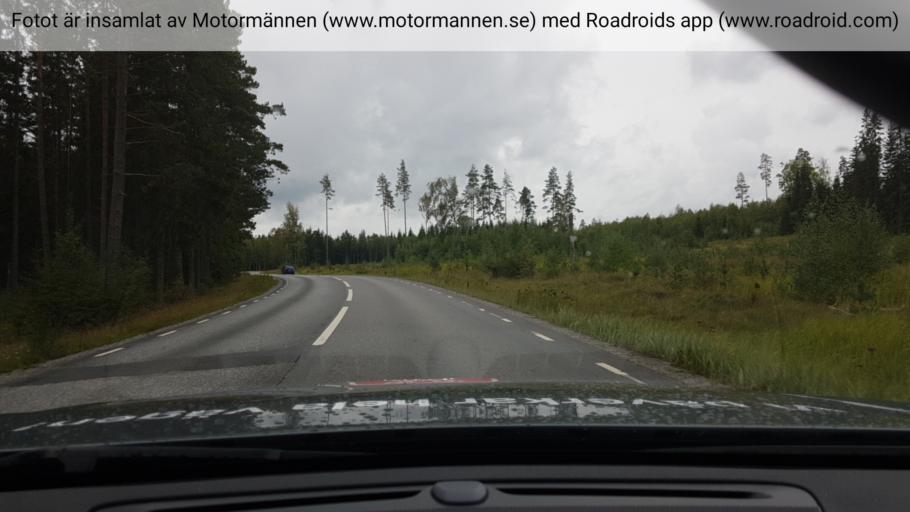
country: SE
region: Stockholm
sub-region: Botkyrka Kommun
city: Tullinge
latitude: 59.1476
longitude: 17.9306
